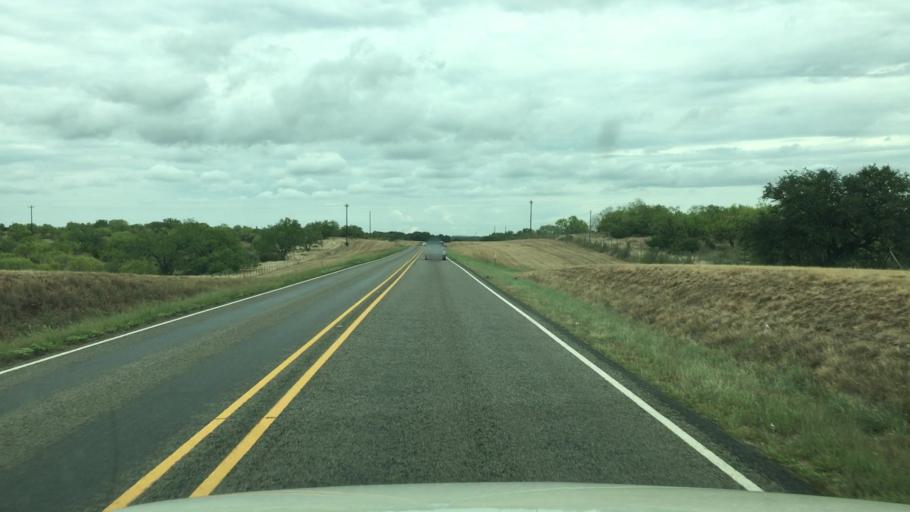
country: US
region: Texas
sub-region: Llano County
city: Kingsland
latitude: 30.5766
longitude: -98.4929
